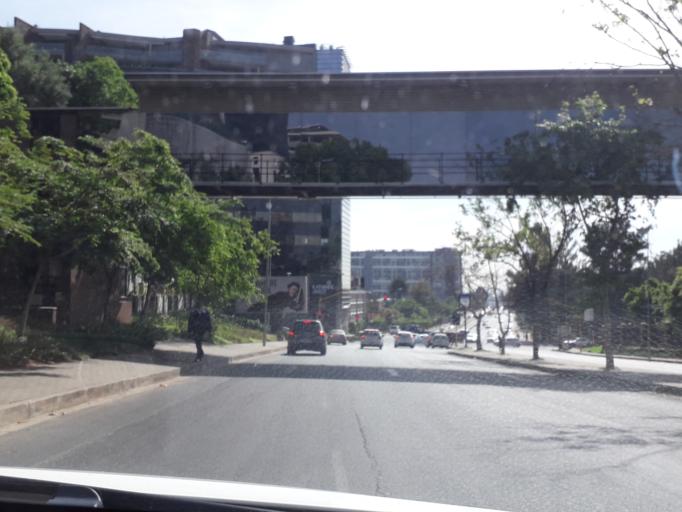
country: ZA
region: Gauteng
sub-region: City of Johannesburg Metropolitan Municipality
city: Johannesburg
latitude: -26.1094
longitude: 28.0585
